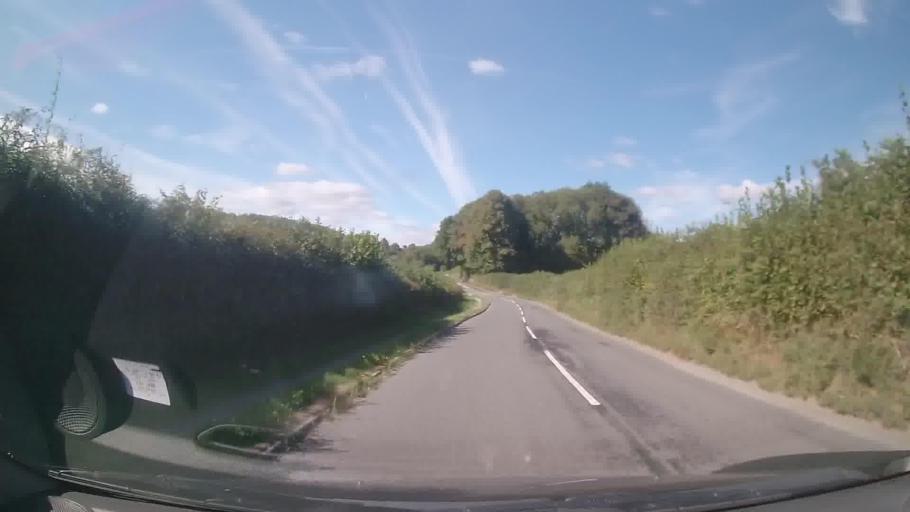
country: GB
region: Wales
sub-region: Sir Powys
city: Hay
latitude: 52.0824
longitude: -3.1400
